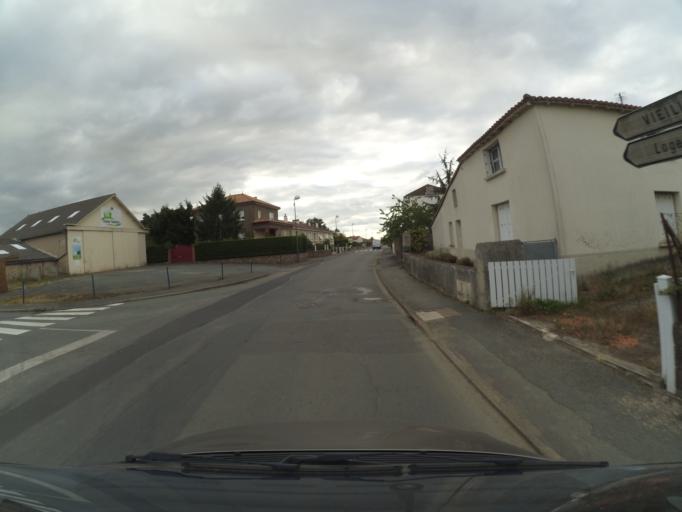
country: FR
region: Pays de la Loire
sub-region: Departement de la Vendee
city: Saint-Andre-Treize-Voies
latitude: 46.9099
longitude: -1.3784
